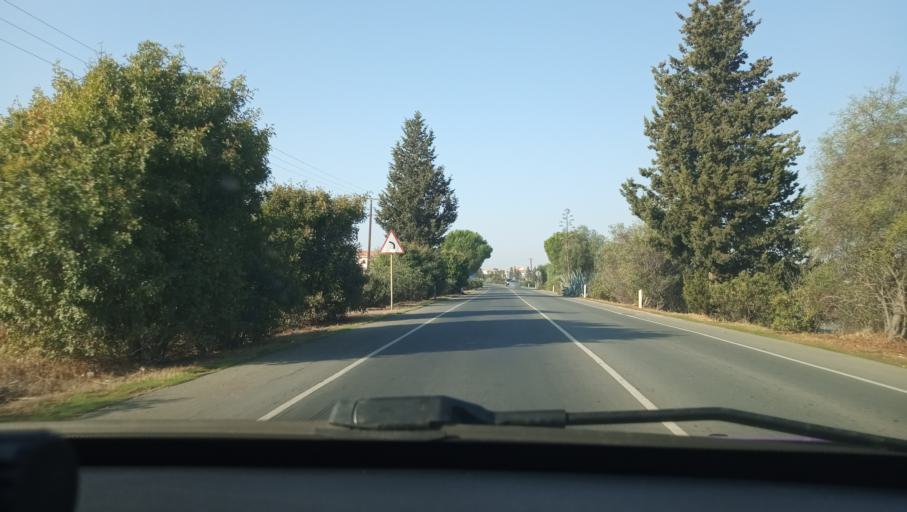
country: CY
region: Lefkosia
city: Kato Deftera
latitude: 35.0904
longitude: 33.2710
